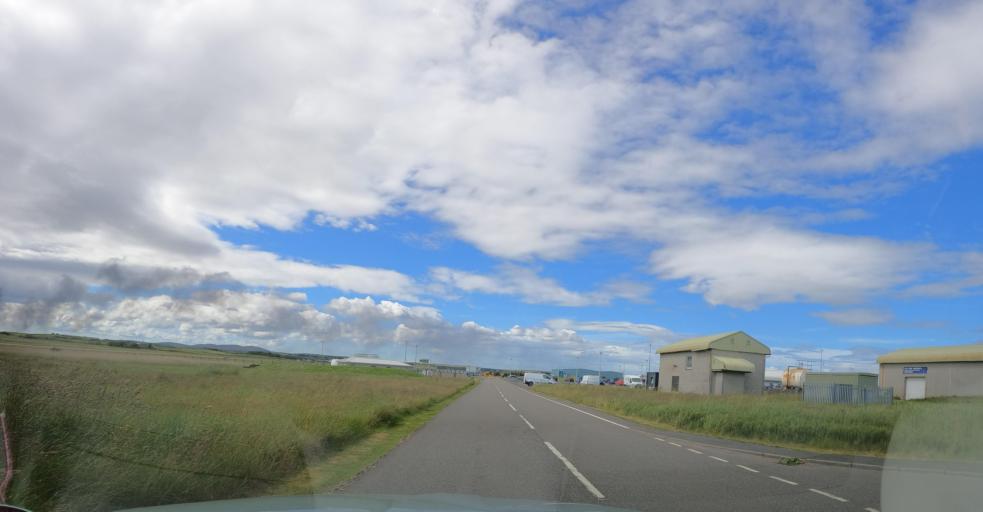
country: GB
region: Scotland
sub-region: Eilean Siar
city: Stornoway
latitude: 58.2123
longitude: -6.3223
